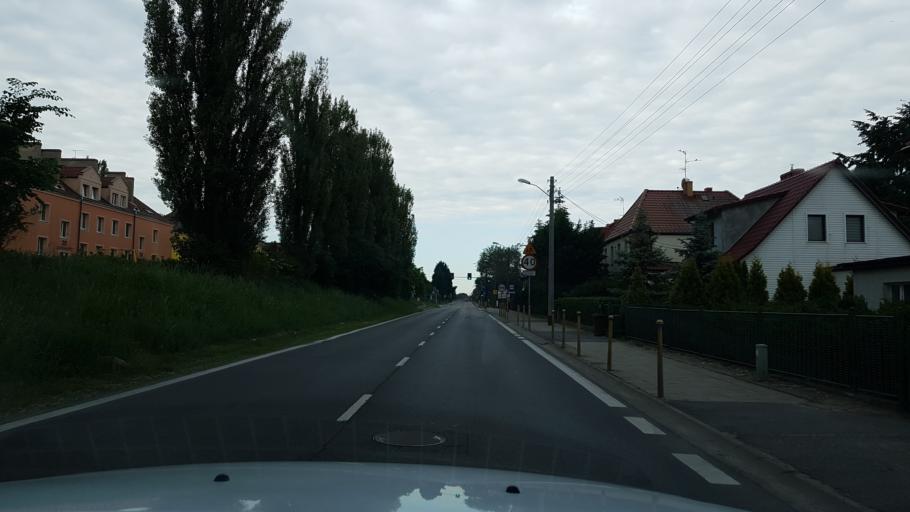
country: PL
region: West Pomeranian Voivodeship
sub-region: Szczecin
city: Szczecin
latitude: 53.3485
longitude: 14.5680
